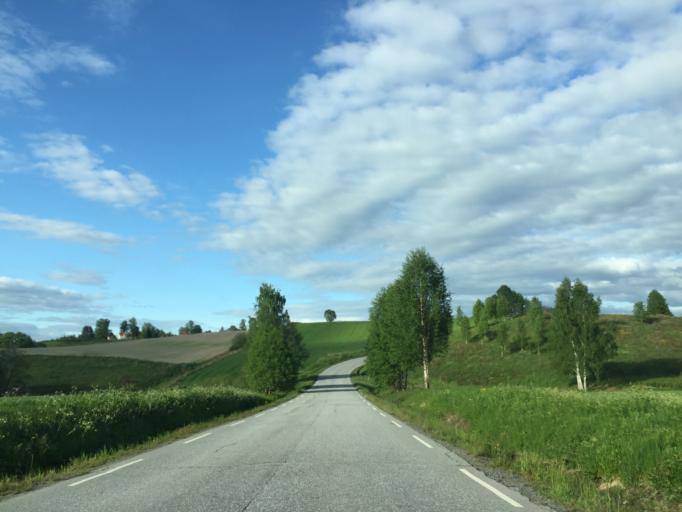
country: NO
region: Akershus
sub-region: Nes
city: Auli
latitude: 60.0076
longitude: 11.3088
